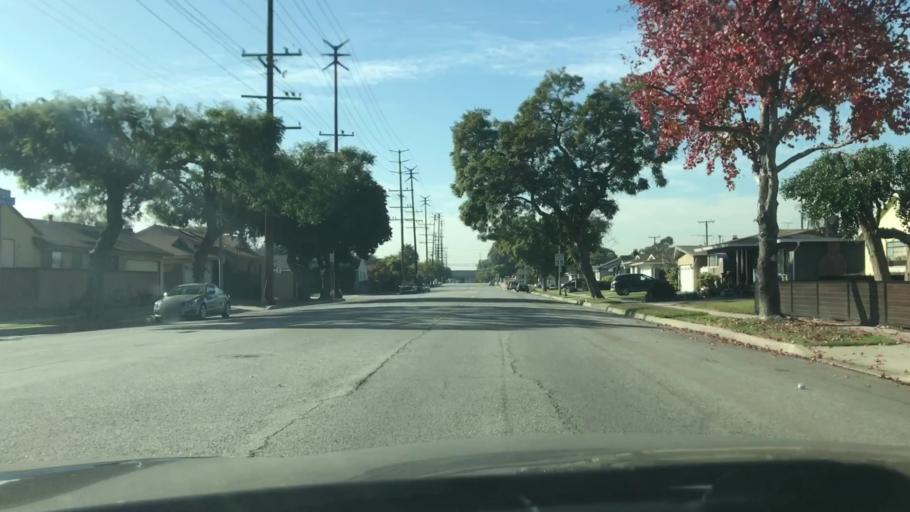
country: US
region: California
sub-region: Orange County
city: Rossmoor
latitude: 33.7956
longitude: -118.1002
